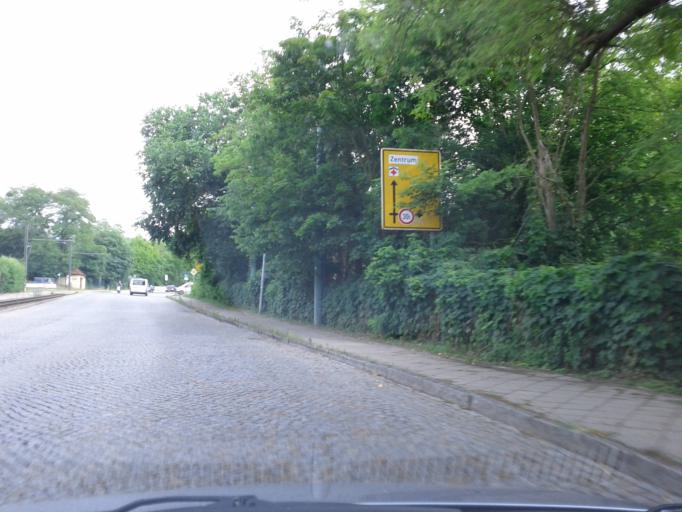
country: DE
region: Brandenburg
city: Woltersdorf
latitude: 52.4737
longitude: 13.7746
